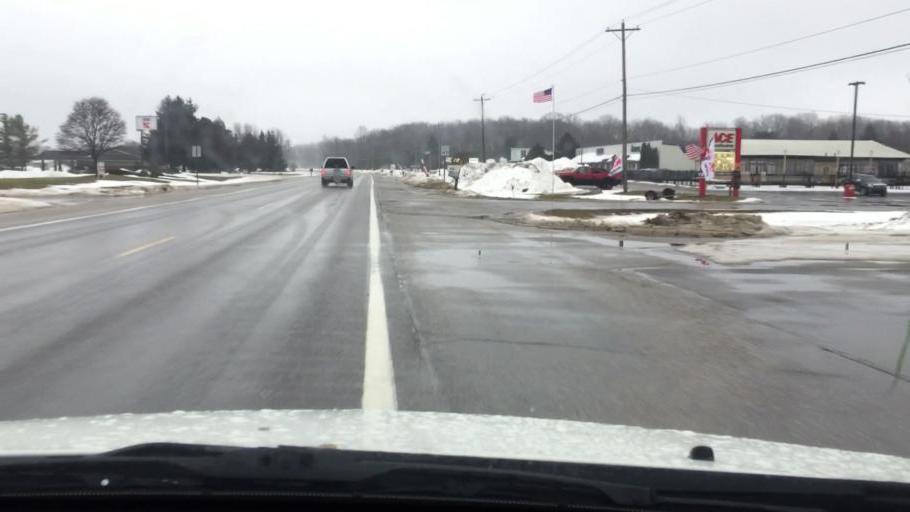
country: US
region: Michigan
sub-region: Charlevoix County
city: Charlevoix
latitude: 45.2998
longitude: -85.2564
